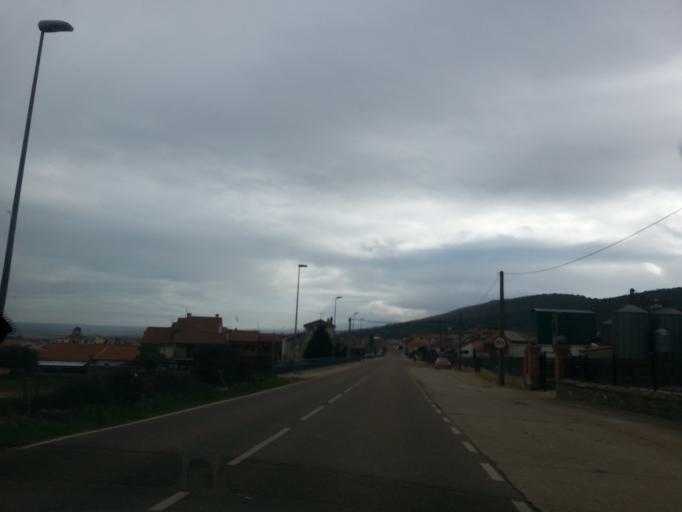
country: ES
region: Castille and Leon
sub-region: Provincia de Salamanca
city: Tamames
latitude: 40.6589
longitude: -6.1122
